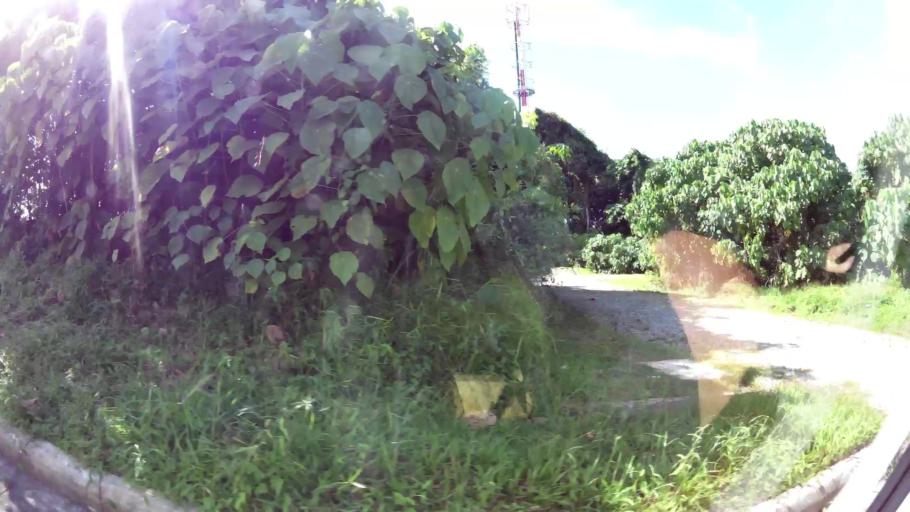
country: BN
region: Brunei and Muara
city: Bandar Seri Begawan
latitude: 4.9562
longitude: 114.9446
